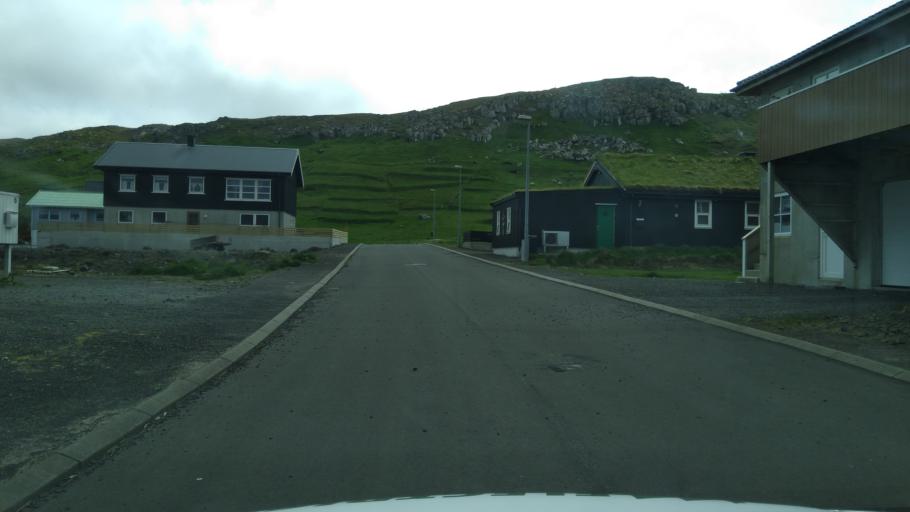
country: FO
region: Sandoy
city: Sandur
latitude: 61.9044
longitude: -6.8920
